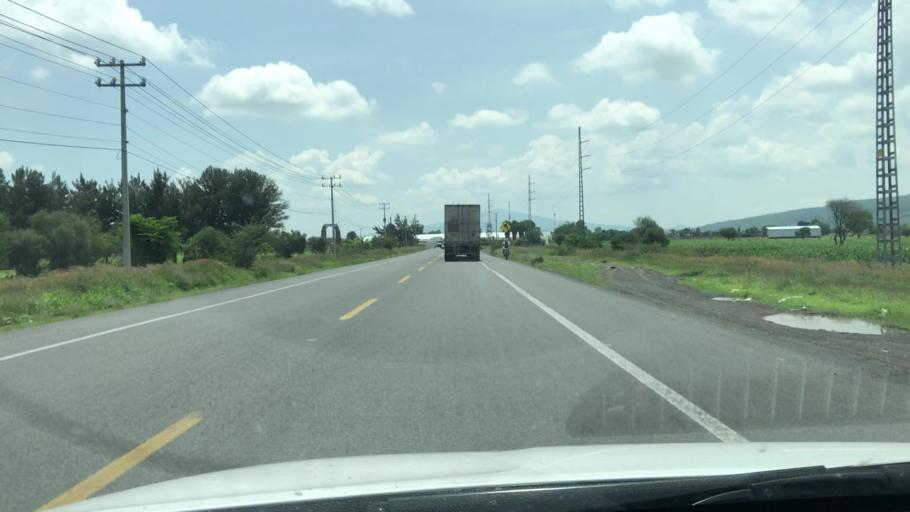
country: MX
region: Michoacan
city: Tanhuato de Guerrero
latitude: 20.2821
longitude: -102.3473
